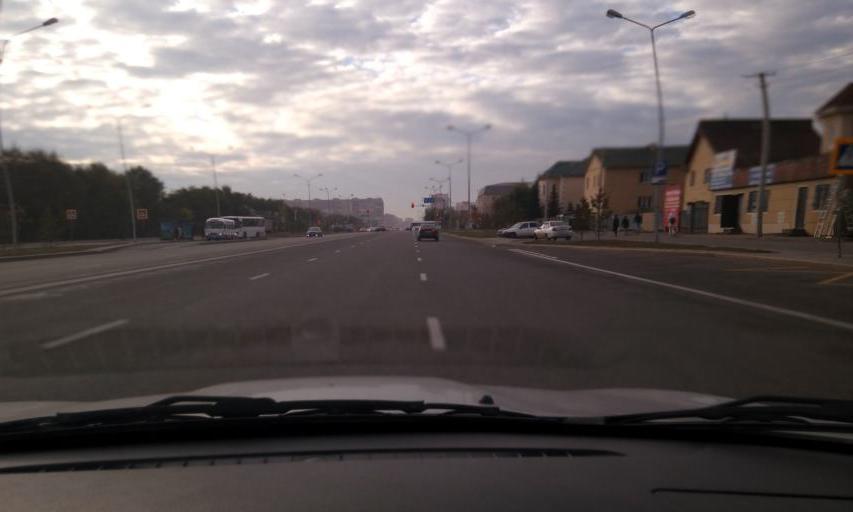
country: KZ
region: Astana Qalasy
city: Astana
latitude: 51.1391
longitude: 71.4898
